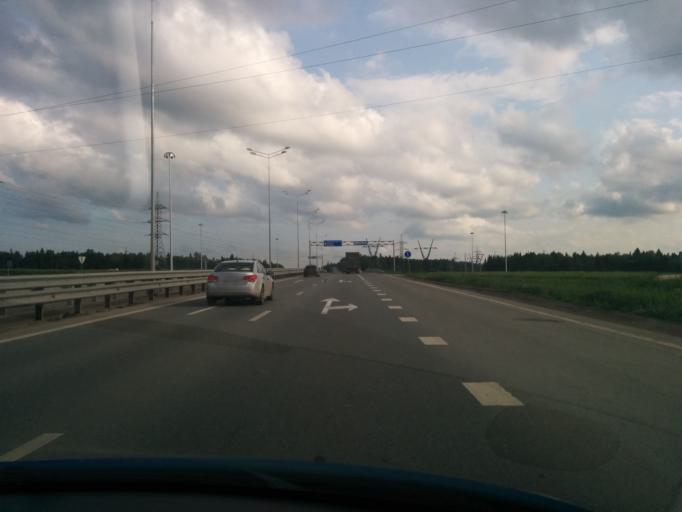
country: RU
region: Perm
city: Novyye Lyady
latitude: 58.0467
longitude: 56.4299
